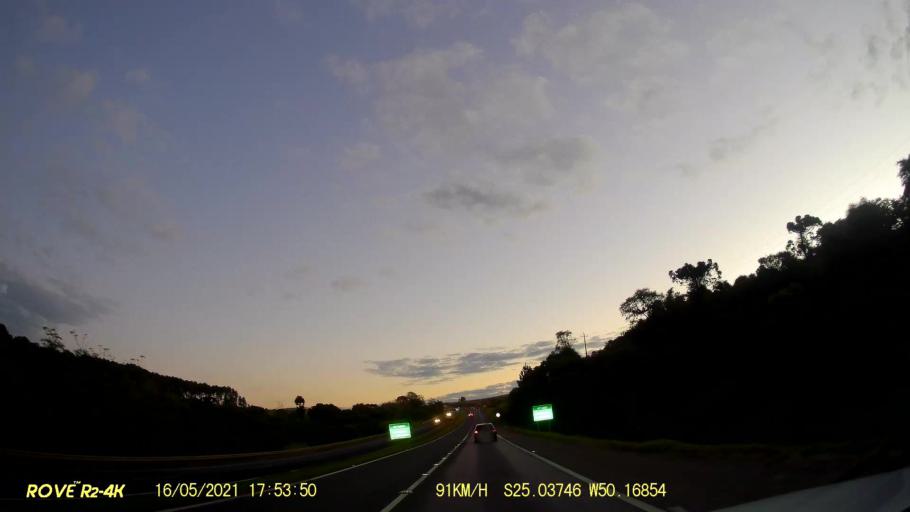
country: BR
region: Parana
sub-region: Ponta Grossa
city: Ponta Grossa
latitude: -25.0373
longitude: -50.1689
